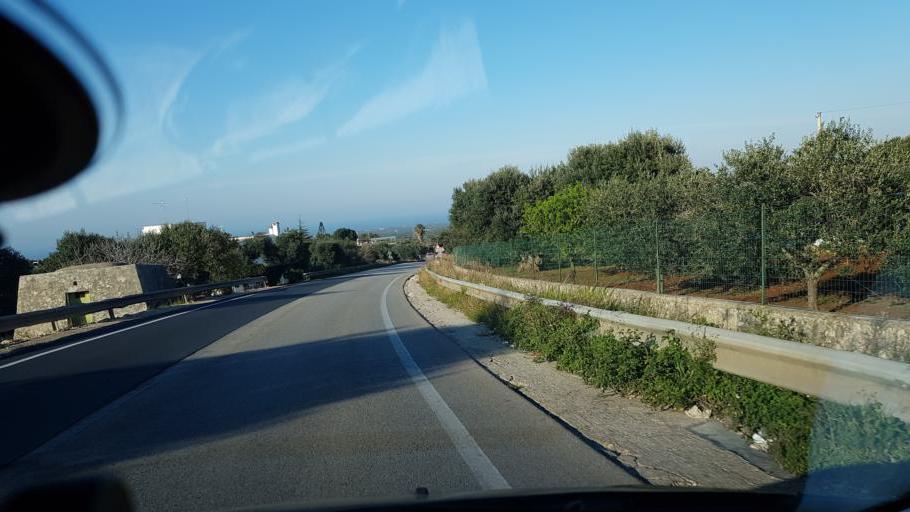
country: IT
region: Apulia
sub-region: Provincia di Brindisi
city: Ostuni
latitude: 40.7317
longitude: 17.5903
